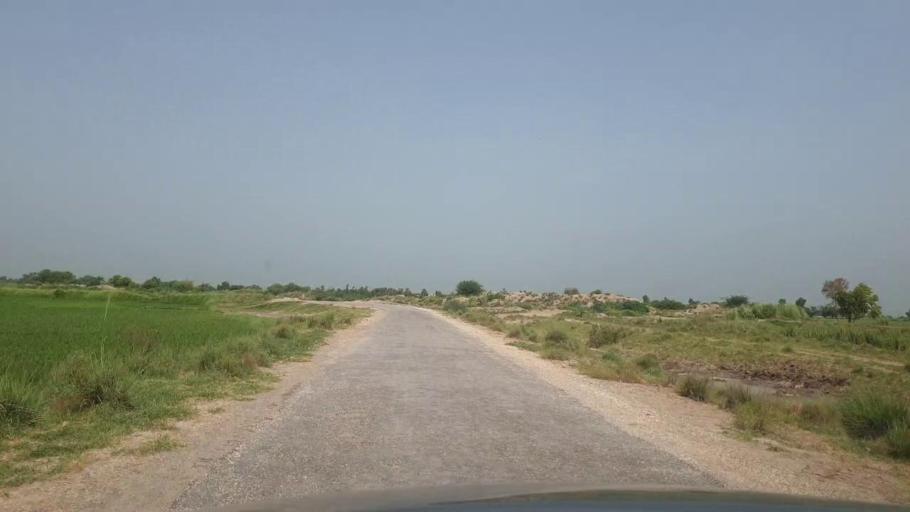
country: PK
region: Sindh
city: Madeji
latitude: 27.8402
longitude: 68.4406
